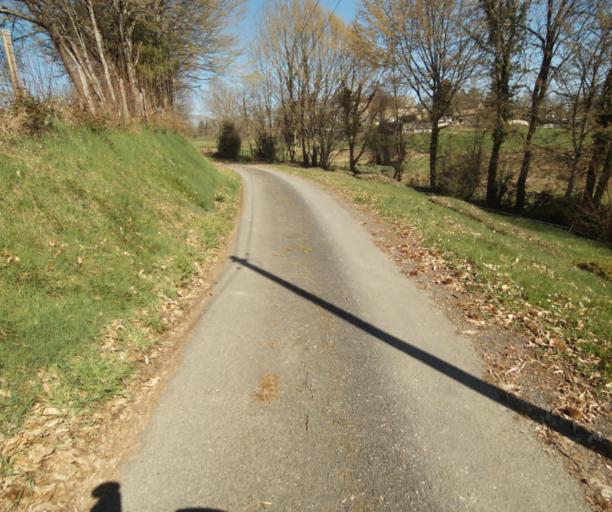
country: FR
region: Limousin
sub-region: Departement de la Correze
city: Saint-Mexant
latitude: 45.2978
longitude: 1.6185
